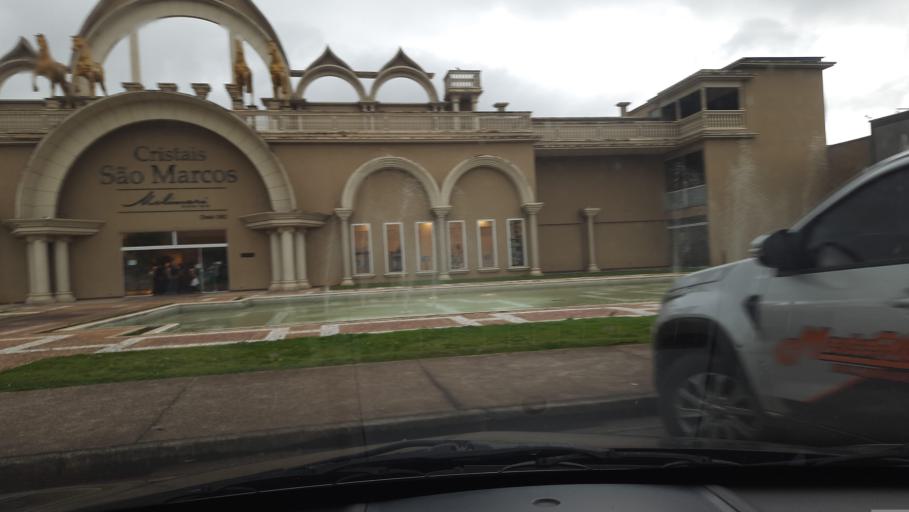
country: BR
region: Minas Gerais
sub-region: Pocos De Caldas
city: Pocos de Caldas
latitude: -21.7791
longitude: -46.6022
